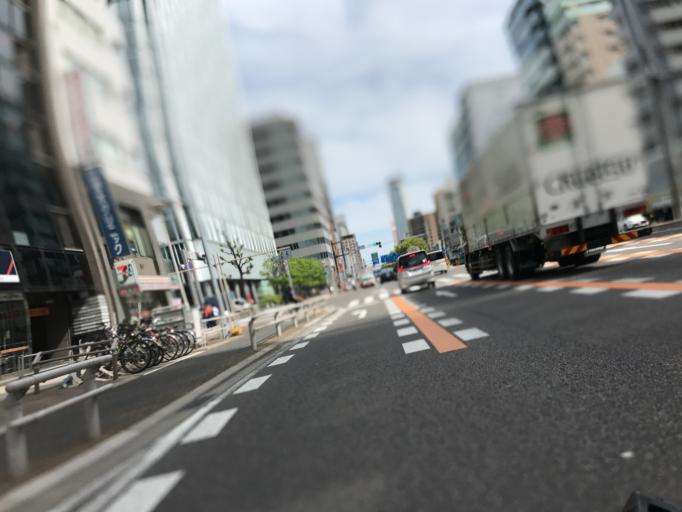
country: JP
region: Aichi
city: Nagoya-shi
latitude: 35.1686
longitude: 136.8975
